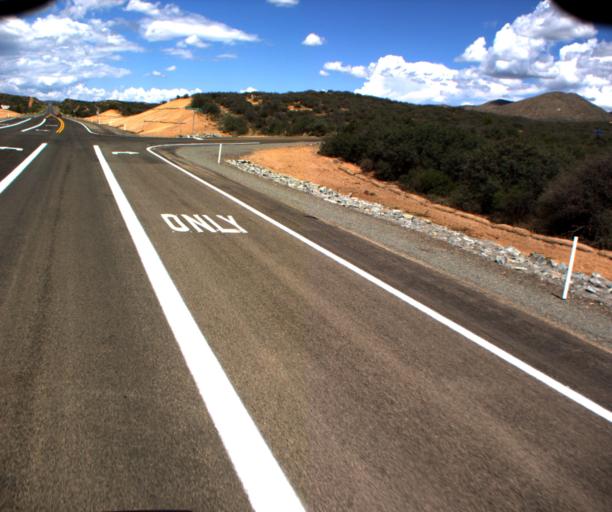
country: US
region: Arizona
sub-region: Yavapai County
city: Dewey-Humboldt
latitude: 34.5250
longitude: -112.0825
